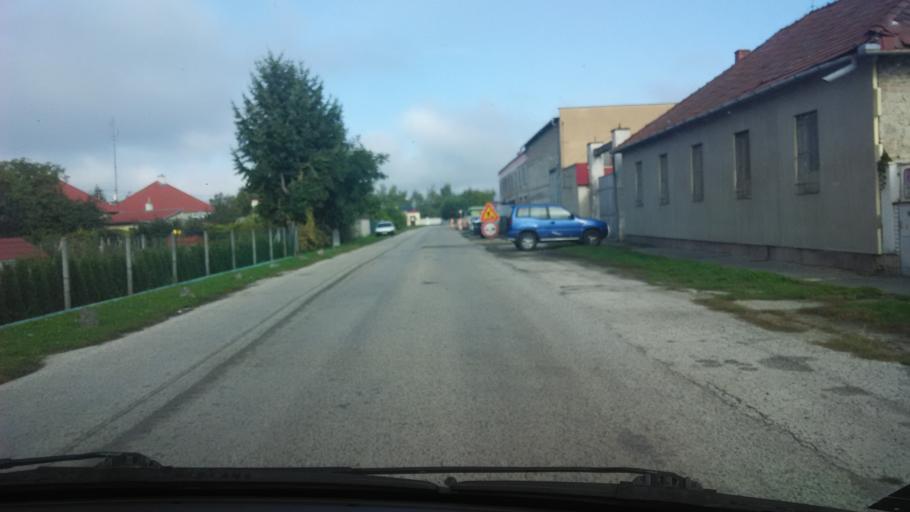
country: SK
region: Nitriansky
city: Levice
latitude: 48.2109
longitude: 18.5890
